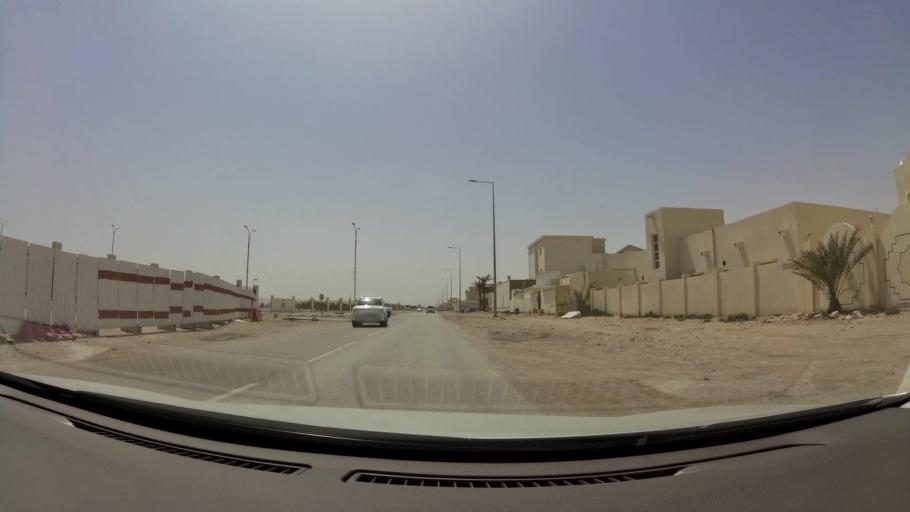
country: QA
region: Baladiyat Umm Salal
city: Umm Salal Muhammad
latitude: 25.3732
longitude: 51.4790
